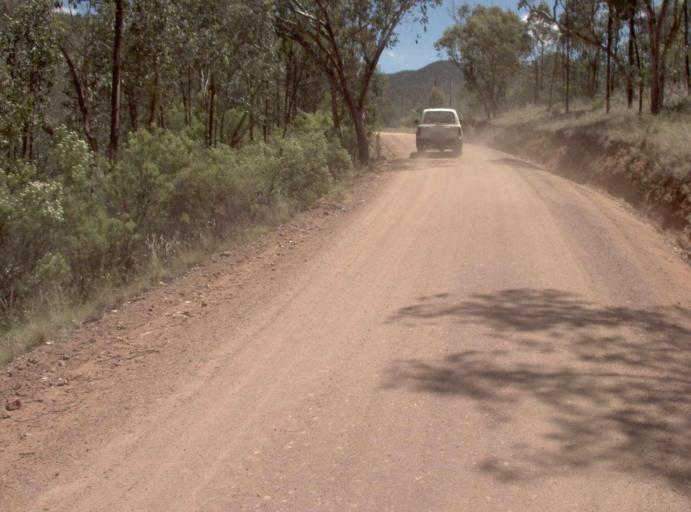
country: AU
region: New South Wales
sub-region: Snowy River
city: Jindabyne
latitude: -36.9264
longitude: 148.3815
